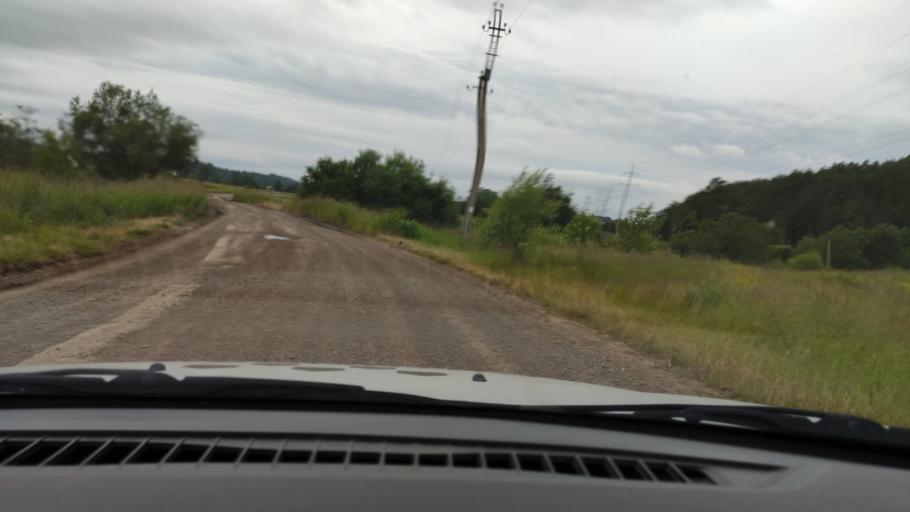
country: RU
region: Perm
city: Orda
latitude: 57.3020
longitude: 56.6302
